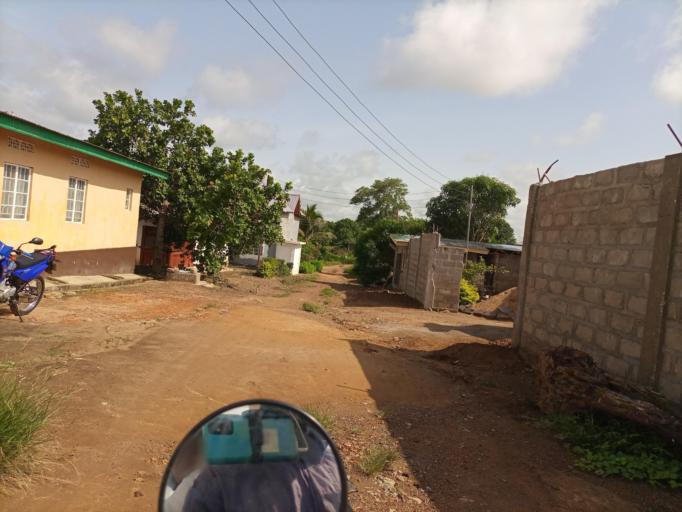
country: SL
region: Southern Province
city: Bo
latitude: 7.9675
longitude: -11.7636
